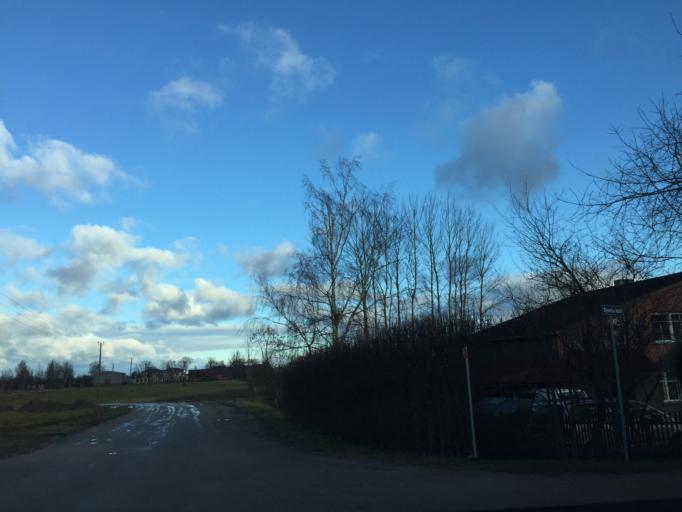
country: LV
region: Valmieras Rajons
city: Valmiera
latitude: 57.5366
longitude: 25.3868
